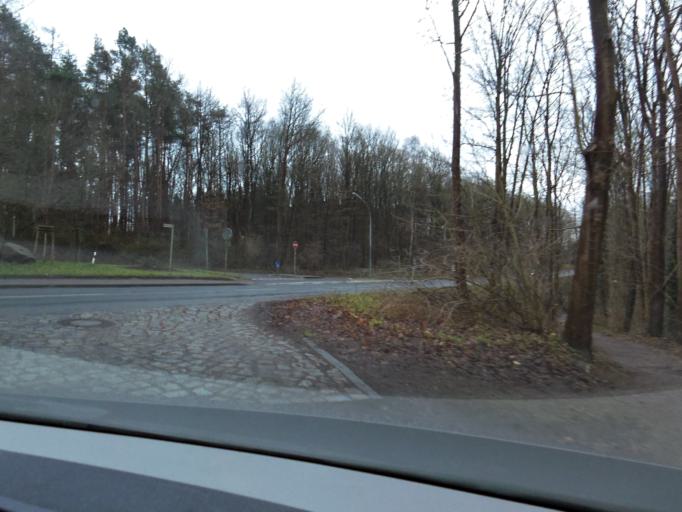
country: DE
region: Schleswig-Holstein
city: Ratzeburg
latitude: 53.7046
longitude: 10.7882
